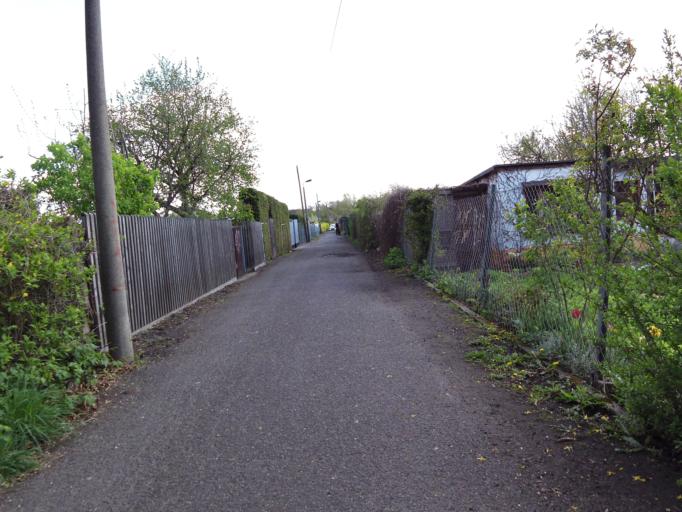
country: DE
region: Saxony
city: Leipzig
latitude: 51.3400
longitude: 12.4229
